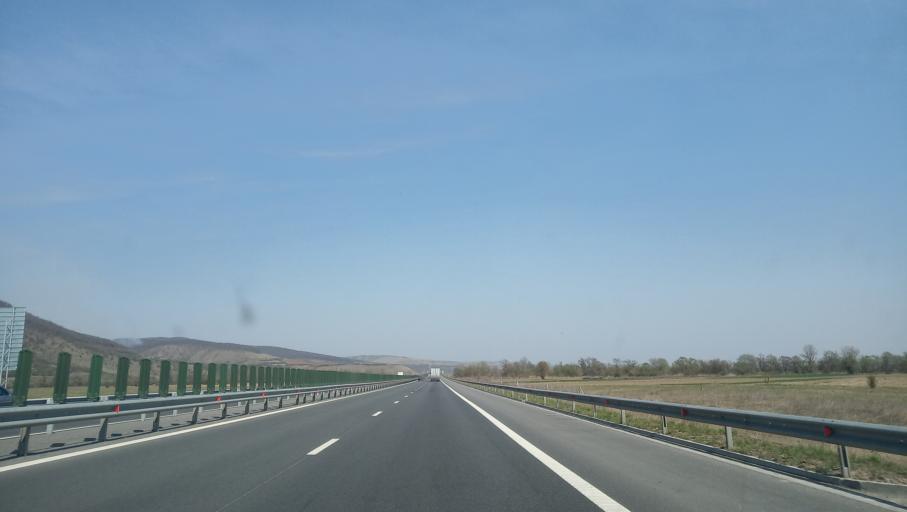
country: RO
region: Alba
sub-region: Comuna Miraslau
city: Miraslau
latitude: 46.3579
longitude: 23.7274
